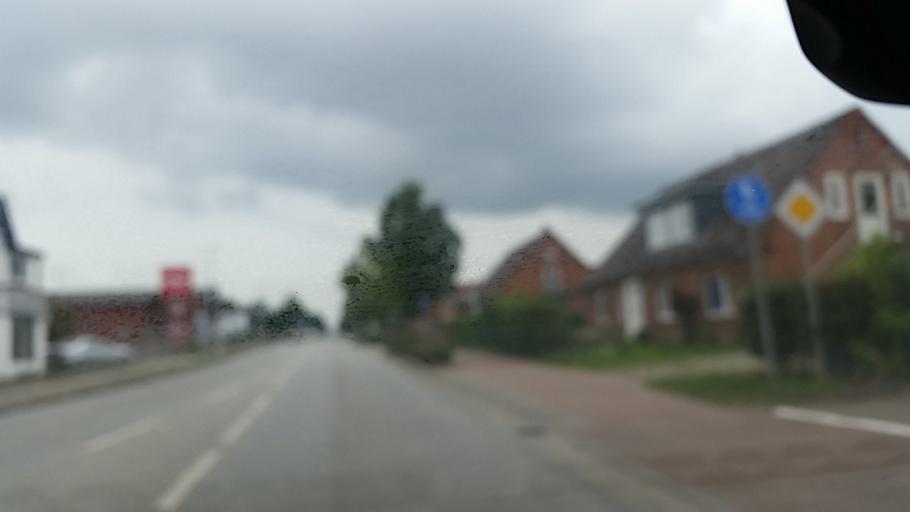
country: DE
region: Schleswig-Holstein
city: Leezen
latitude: 53.8652
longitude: 10.2512
